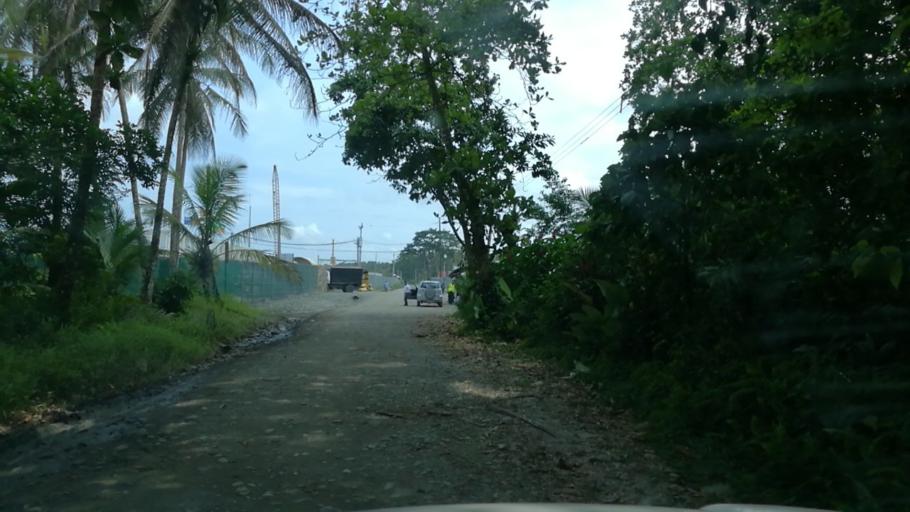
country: CR
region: Limon
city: Limon
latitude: 10.0114
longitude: -83.1097
